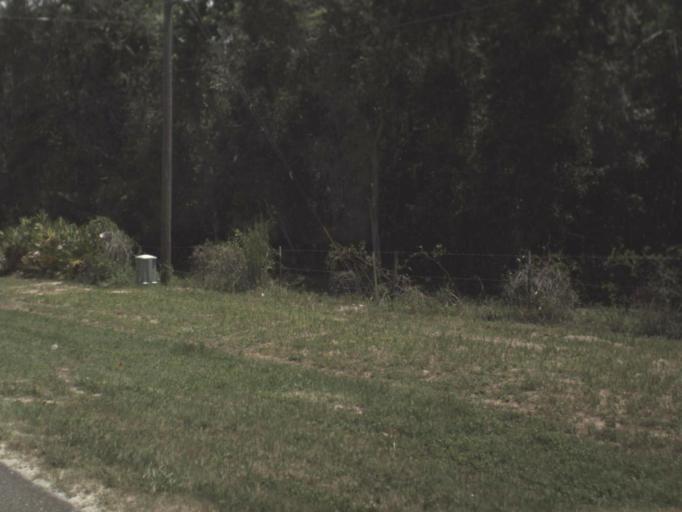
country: US
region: Florida
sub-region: Clay County
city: Keystone Heights
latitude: 29.7250
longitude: -82.0467
